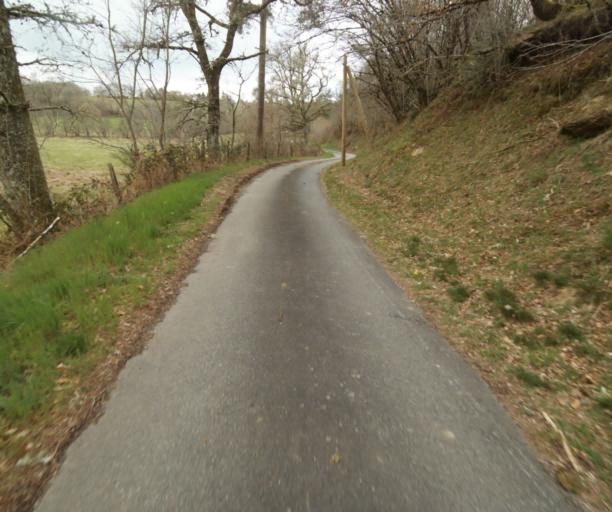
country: FR
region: Limousin
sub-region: Departement de la Correze
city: Correze
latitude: 45.3113
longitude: 1.8917
